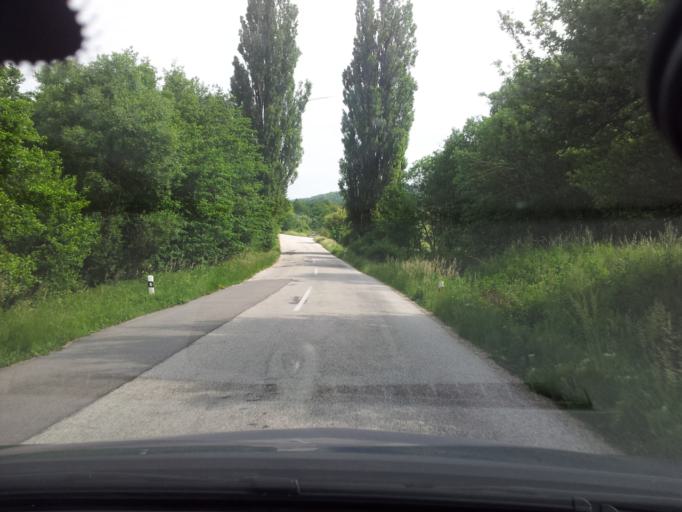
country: SK
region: Nitriansky
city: Zlate Moravce
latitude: 48.5055
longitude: 18.4328
